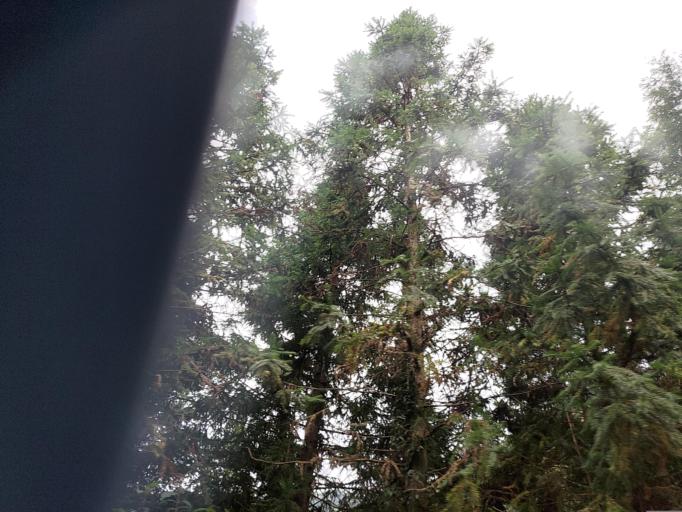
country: TW
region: Taiwan
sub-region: Hsinchu
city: Hsinchu
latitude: 24.6262
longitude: 121.0633
